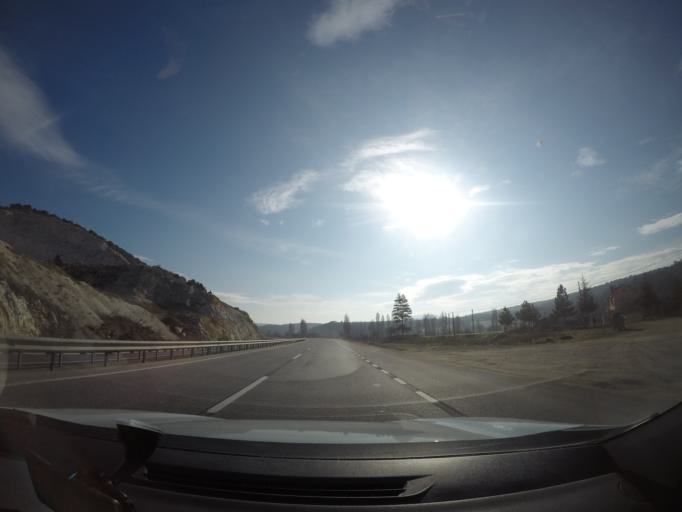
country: TR
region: Bilecik
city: Bozuyuk
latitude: 39.8940
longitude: 29.9657
